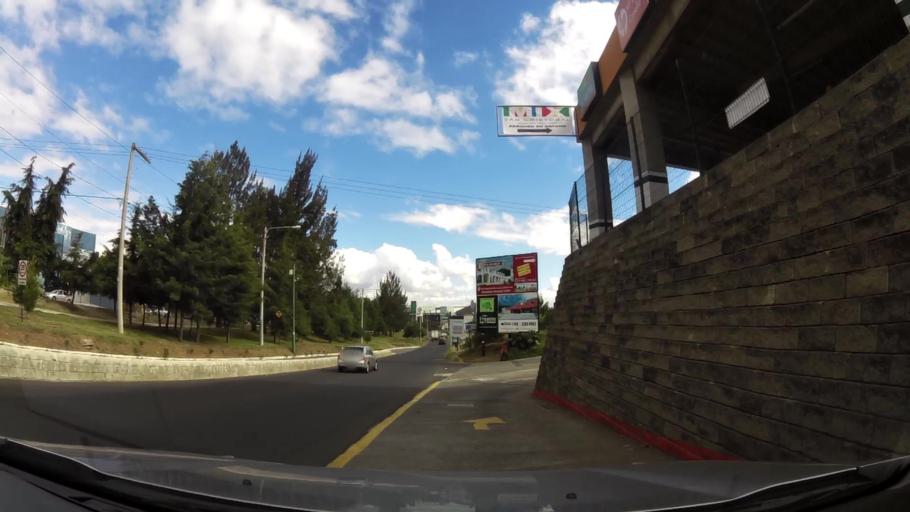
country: GT
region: Guatemala
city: Mixco
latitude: 14.6132
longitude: -90.6002
